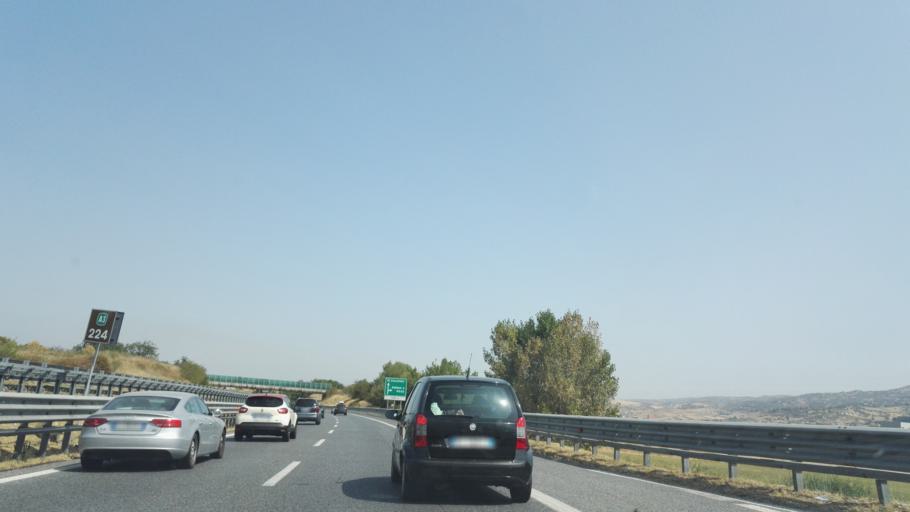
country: IT
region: Calabria
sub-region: Provincia di Cosenza
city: Stazione Montalto-Coretto
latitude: 39.4119
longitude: 16.2450
